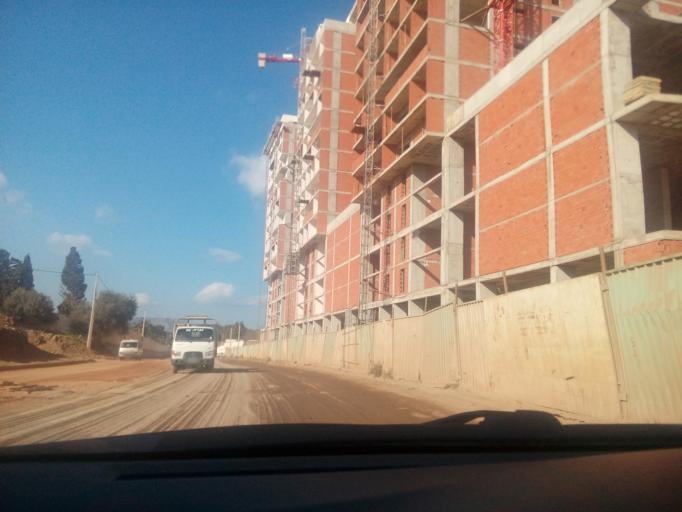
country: DZ
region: Oran
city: Es Senia
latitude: 35.6796
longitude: -0.6057
